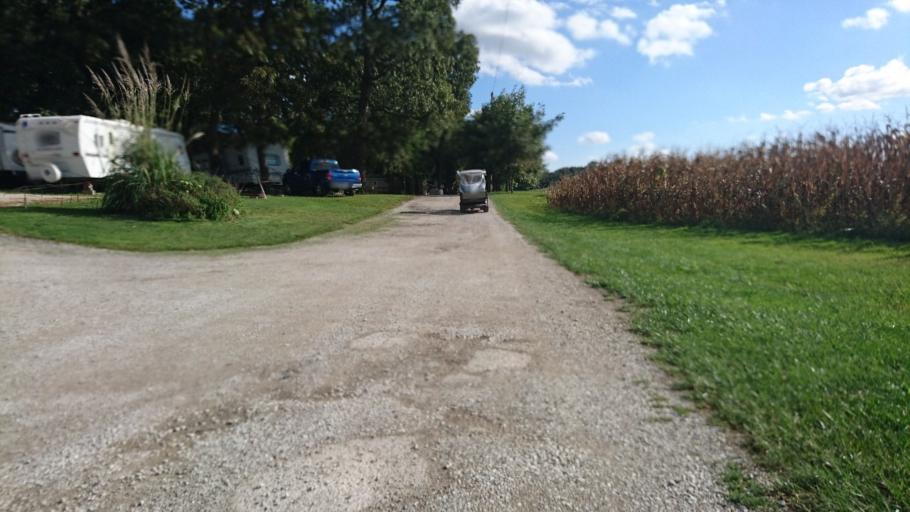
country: US
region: Illinois
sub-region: Macoupin County
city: Mount Olive
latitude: 38.9808
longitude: -89.6990
